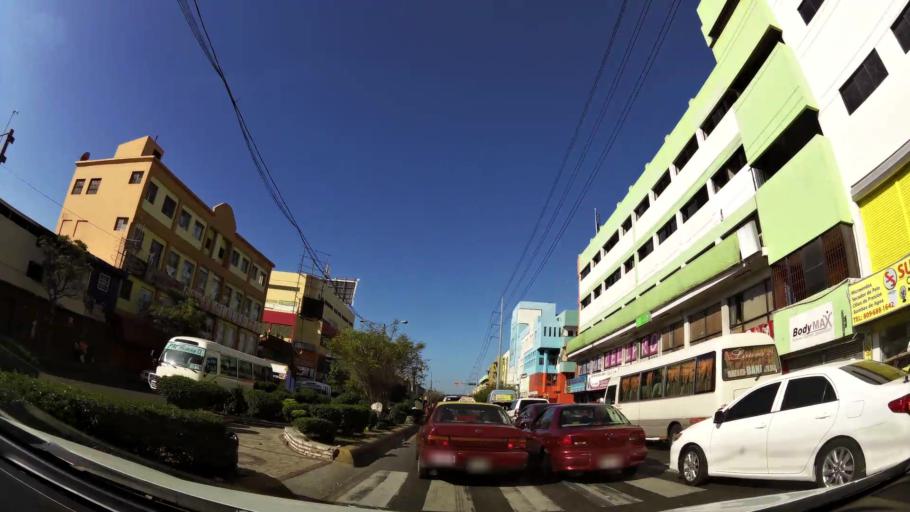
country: DO
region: Nacional
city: San Carlos
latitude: 18.4797
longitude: -69.8884
